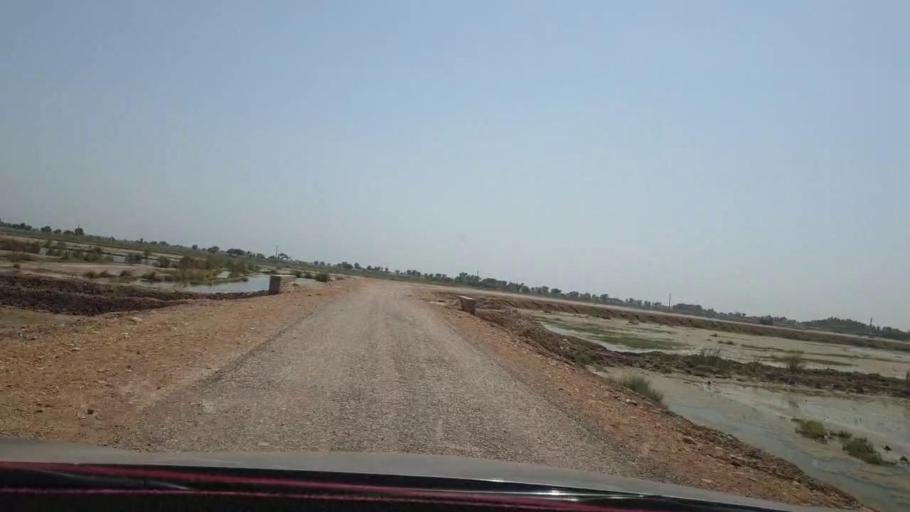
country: PK
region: Sindh
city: Warah
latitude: 27.5056
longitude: 67.7137
